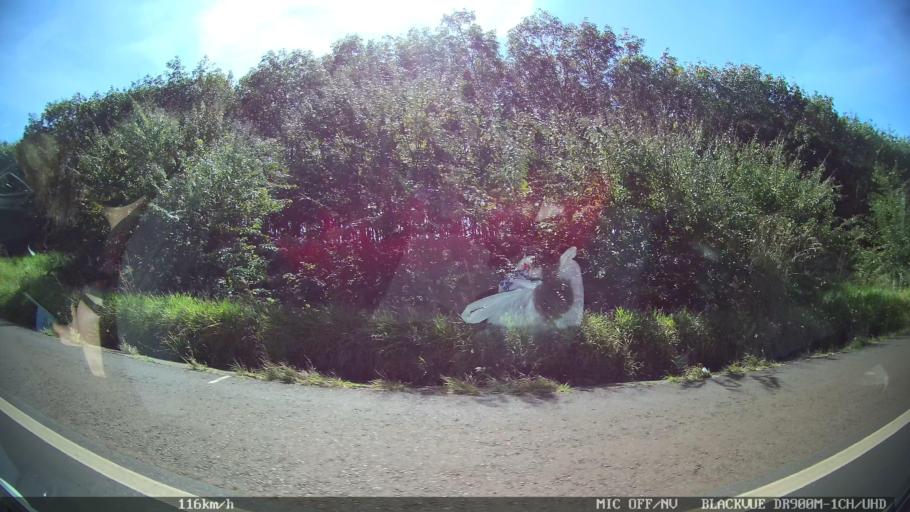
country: BR
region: Sao Paulo
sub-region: Franca
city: Franca
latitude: -20.5589
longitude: -47.5418
